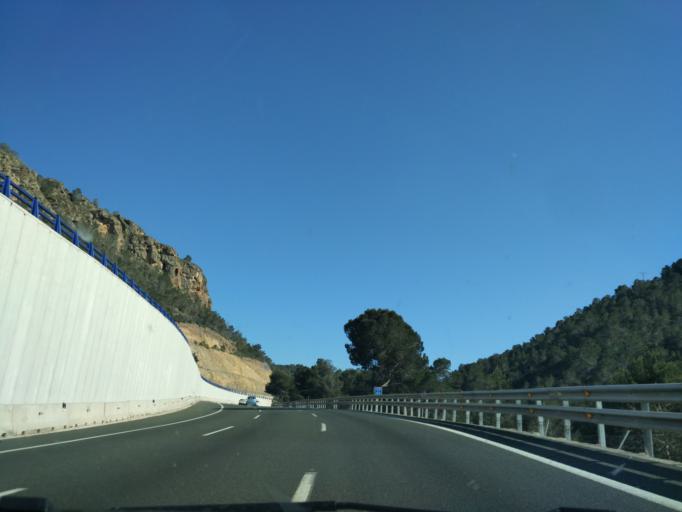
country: ES
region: Murcia
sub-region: Murcia
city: Murcia
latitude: 37.9040
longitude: -1.1458
